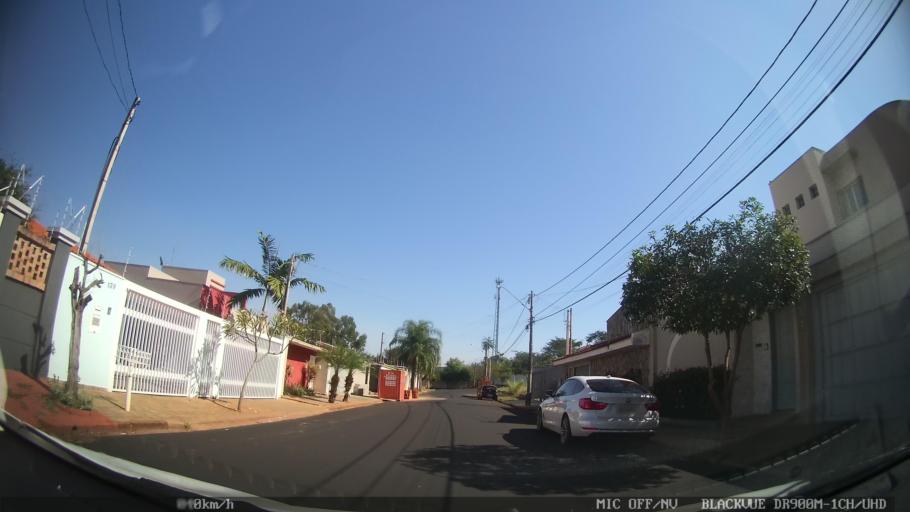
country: BR
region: Sao Paulo
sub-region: Ribeirao Preto
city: Ribeirao Preto
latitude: -21.2098
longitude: -47.7756
